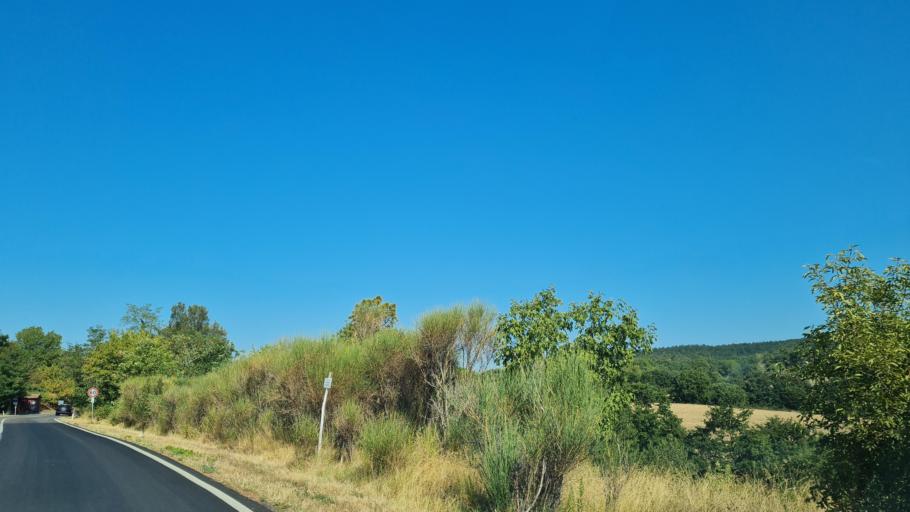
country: IT
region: Tuscany
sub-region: Provincia di Siena
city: Chianciano Terme
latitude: 43.0403
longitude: 11.8075
